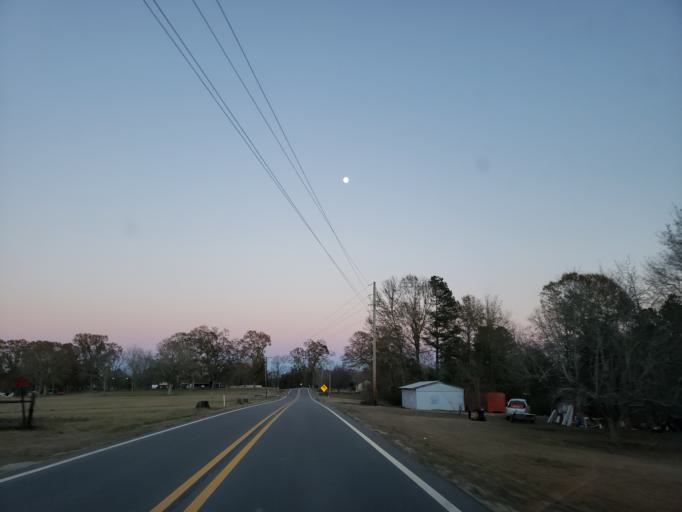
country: US
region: Mississippi
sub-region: Jones County
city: Ellisville
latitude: 31.5821
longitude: -89.2460
